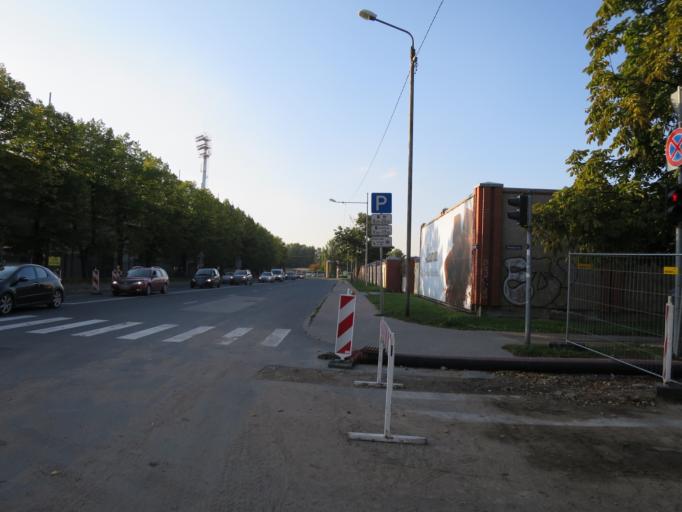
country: LV
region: Riga
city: Riga
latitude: 56.9615
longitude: 24.1182
